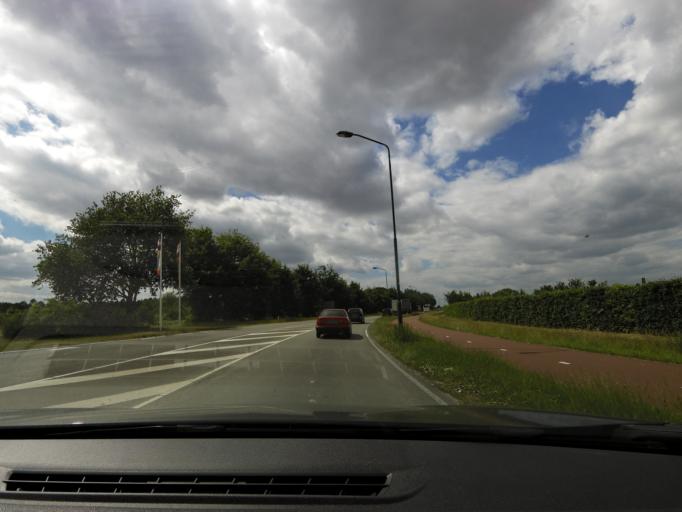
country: NL
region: North Brabant
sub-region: Gemeente Dongen
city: Dongen
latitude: 51.6291
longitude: 4.9166
